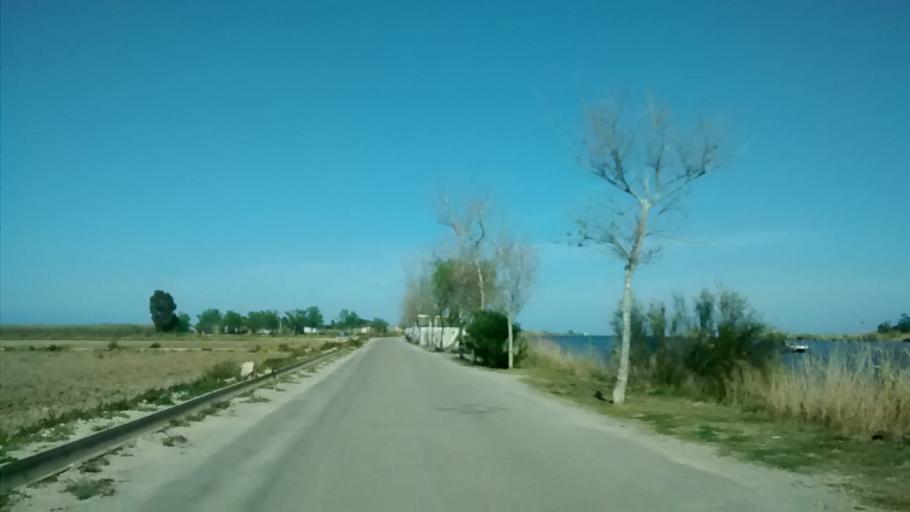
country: ES
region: Catalonia
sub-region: Provincia de Tarragona
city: Deltebre
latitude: 40.7150
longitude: 0.8386
